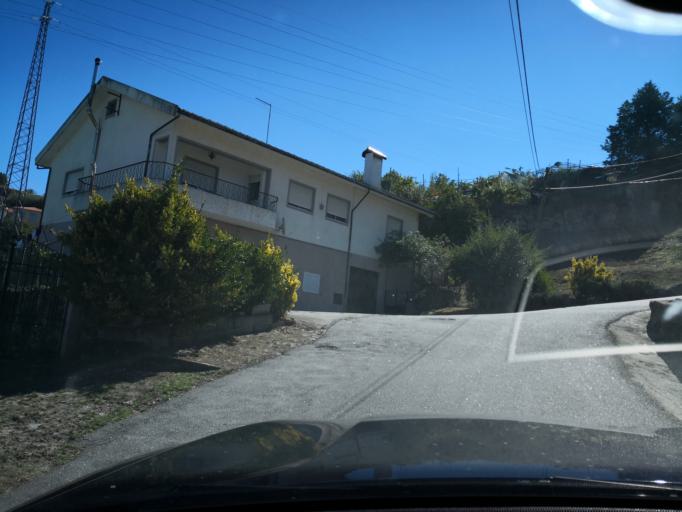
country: PT
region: Vila Real
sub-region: Vila Real
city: Vila Real
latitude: 41.2861
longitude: -7.7615
